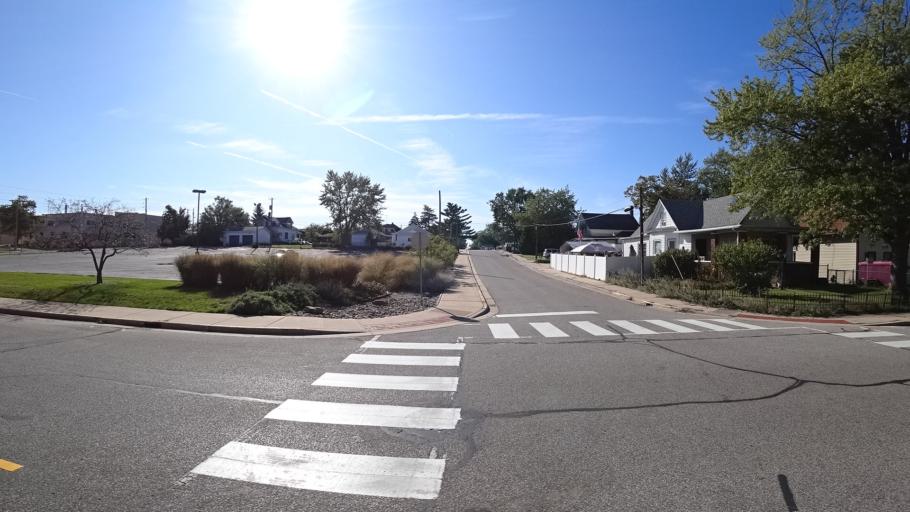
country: US
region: Indiana
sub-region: LaPorte County
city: Michigan City
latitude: 41.7083
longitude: -86.9007
